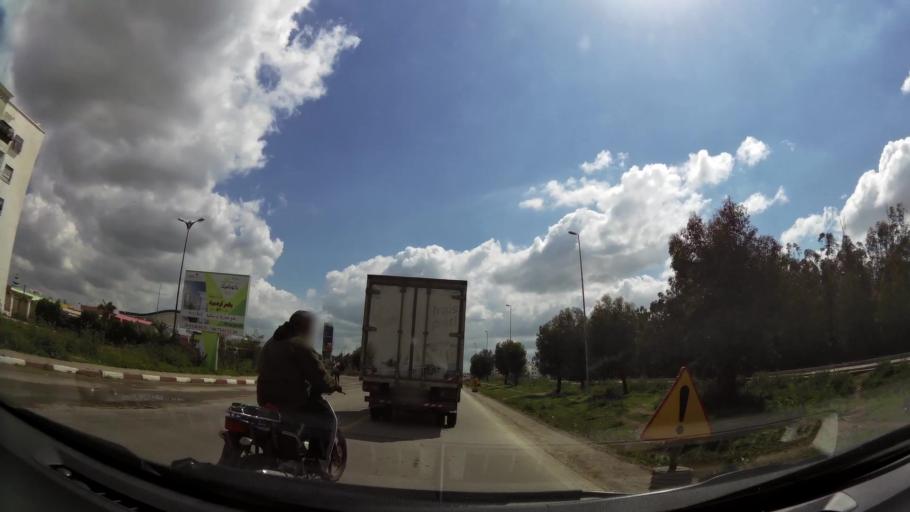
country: MA
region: Chaouia-Ouardigha
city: Nouaseur
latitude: 33.3696
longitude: -7.5430
